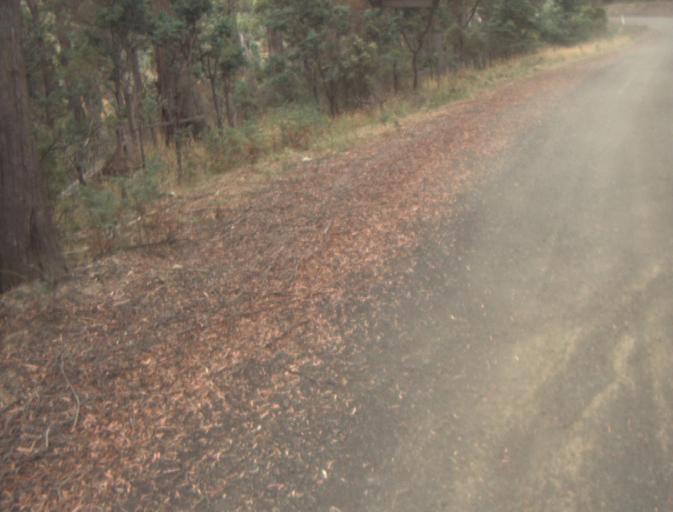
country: AU
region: Tasmania
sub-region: Northern Midlands
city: Evandale
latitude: -41.4830
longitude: 147.5374
